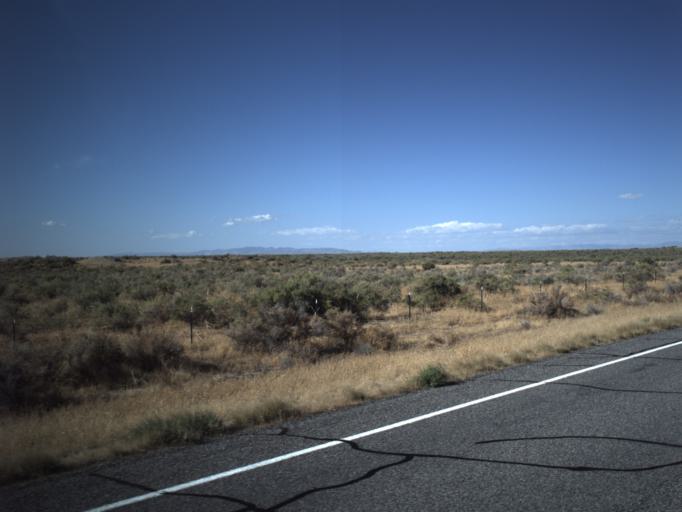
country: US
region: Utah
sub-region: Millard County
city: Delta
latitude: 39.3539
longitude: -112.4416
